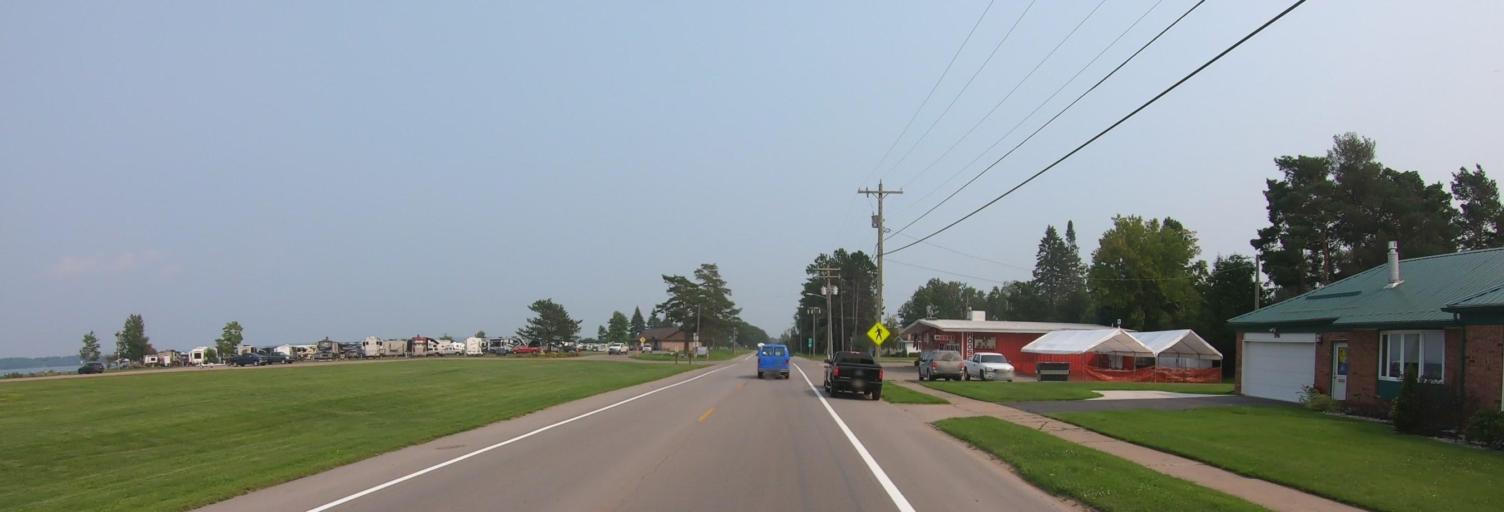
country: US
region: Michigan
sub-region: Chippewa County
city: Sault Ste. Marie
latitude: 46.4888
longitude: -84.3117
